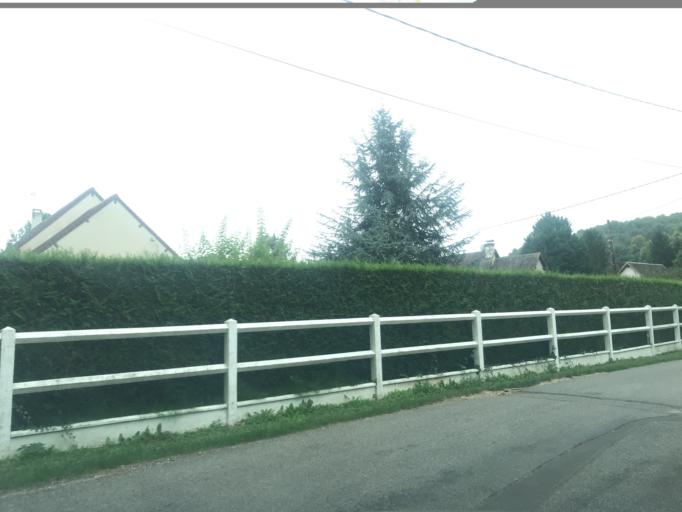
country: FR
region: Haute-Normandie
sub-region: Departement de l'Eure
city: Houlbec-Cocherel
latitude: 49.0743
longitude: 1.2873
